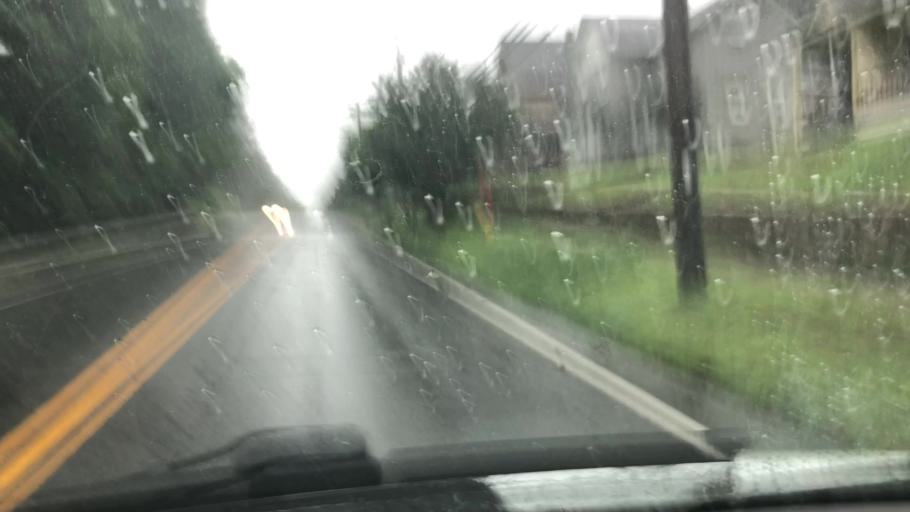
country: US
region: Massachusetts
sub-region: Berkshire County
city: Adams
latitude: 42.6132
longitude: -73.1247
